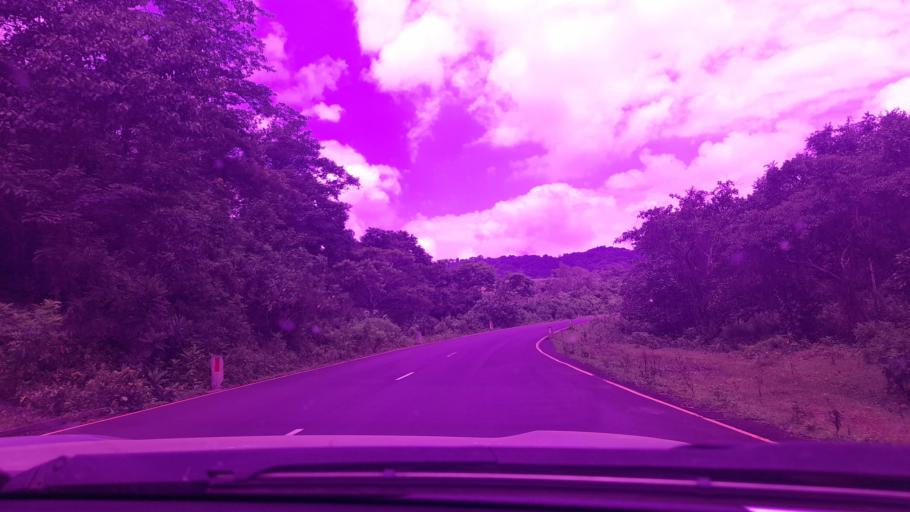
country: ET
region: Oromiya
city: Metu
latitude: 8.3286
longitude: 35.7638
